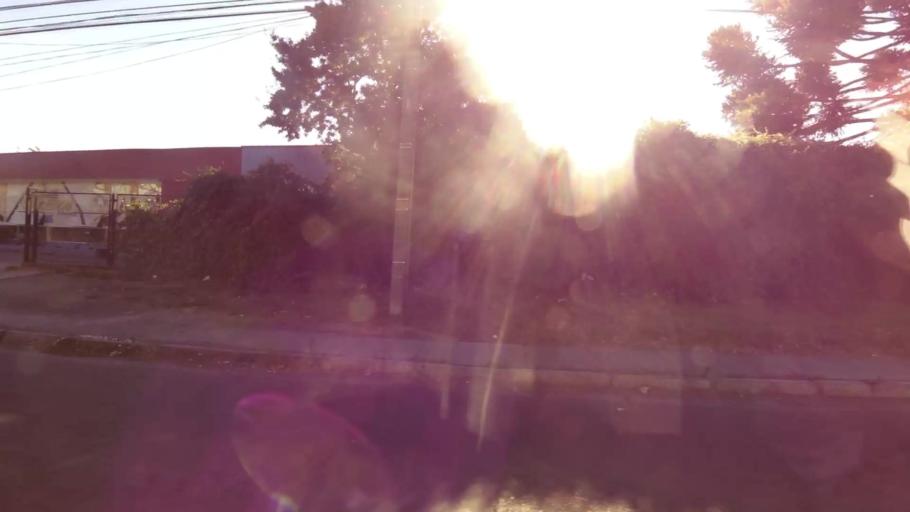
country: CL
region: Biobio
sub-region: Provincia de Concepcion
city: Concepcion
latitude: -36.8371
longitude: -73.1142
